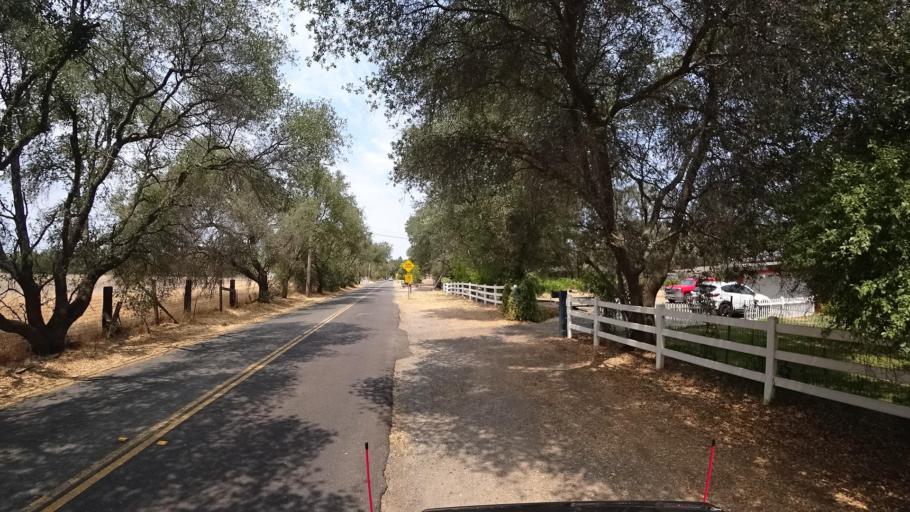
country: US
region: California
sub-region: Placer County
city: Loomis
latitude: 38.8154
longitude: -121.2102
